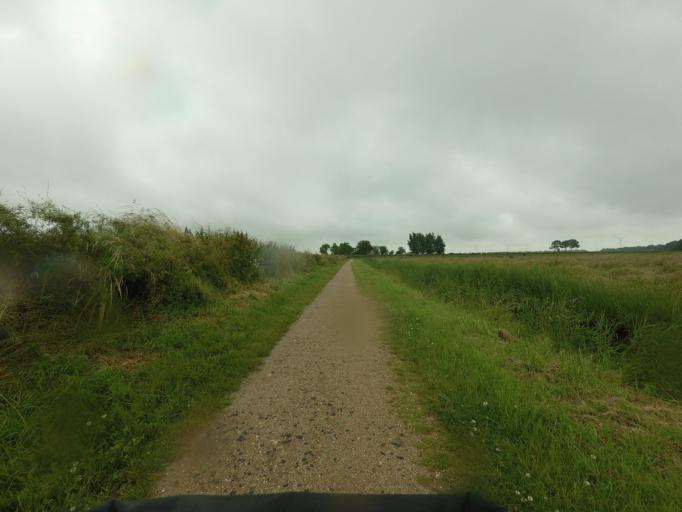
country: NL
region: North Holland
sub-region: Gemeente Opmeer
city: Opmeer
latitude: 52.7490
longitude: 4.9416
